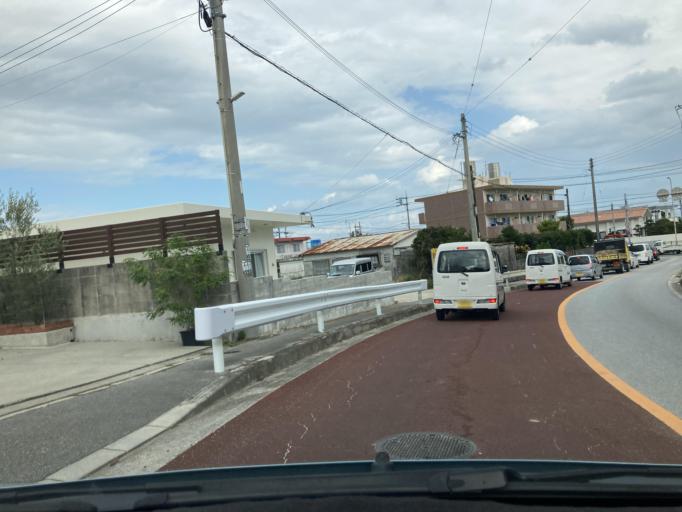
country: JP
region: Okinawa
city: Ginowan
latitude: 26.2541
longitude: 127.7835
